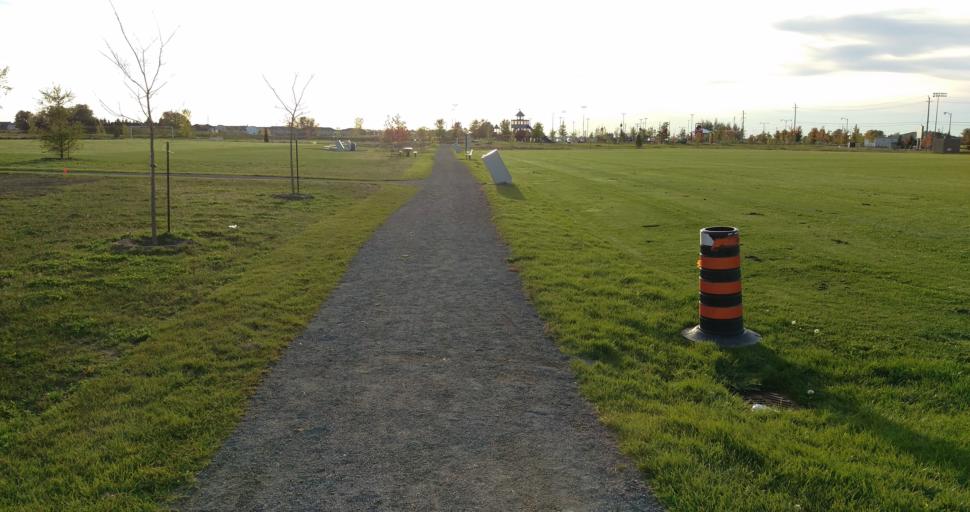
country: CA
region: Ontario
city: Clarence-Rockland
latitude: 45.4661
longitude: -75.4440
